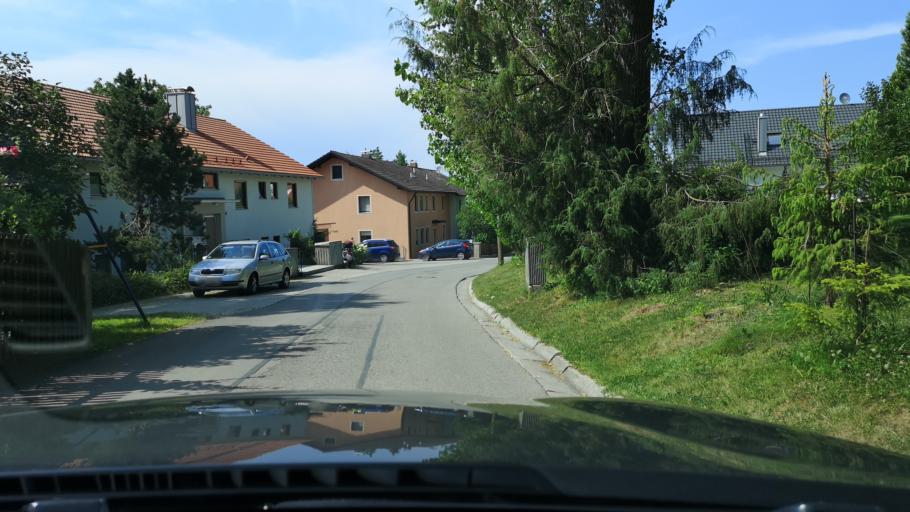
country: DE
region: Bavaria
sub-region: Upper Bavaria
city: Pliening
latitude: 48.1847
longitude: 11.8113
